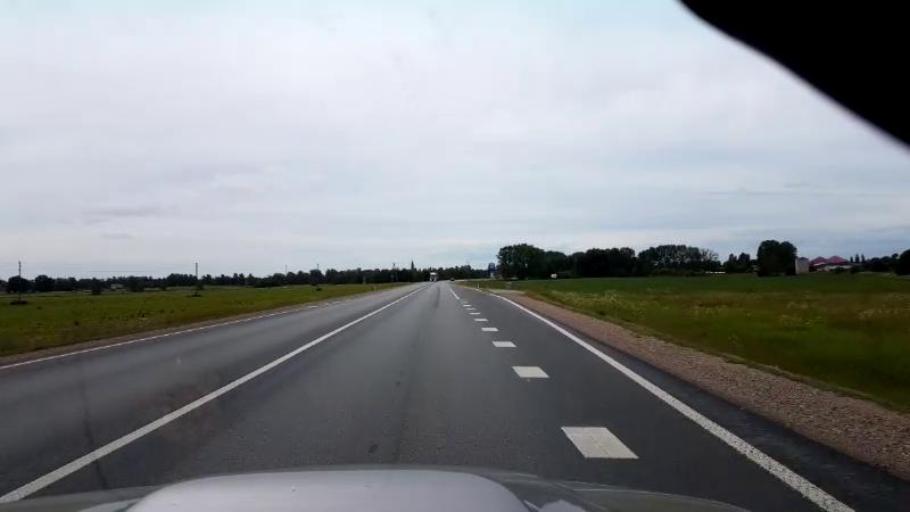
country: LV
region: Lecava
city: Iecava
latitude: 56.6107
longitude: 24.2139
